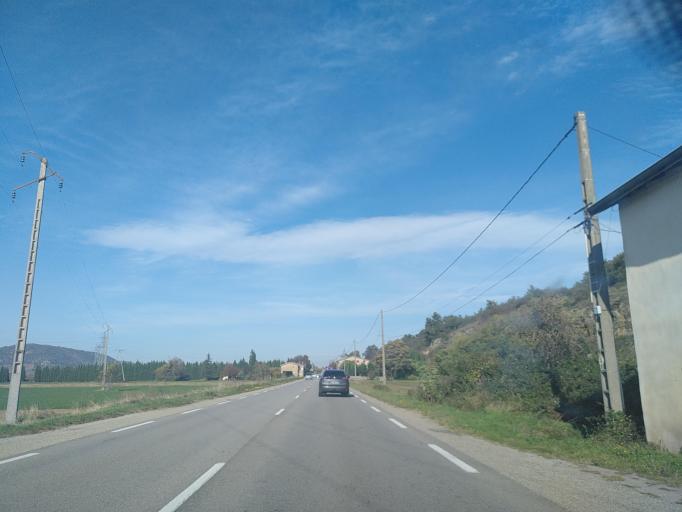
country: FR
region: Rhone-Alpes
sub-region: Departement de la Drome
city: Beausemblant
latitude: 45.2139
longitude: 4.8156
